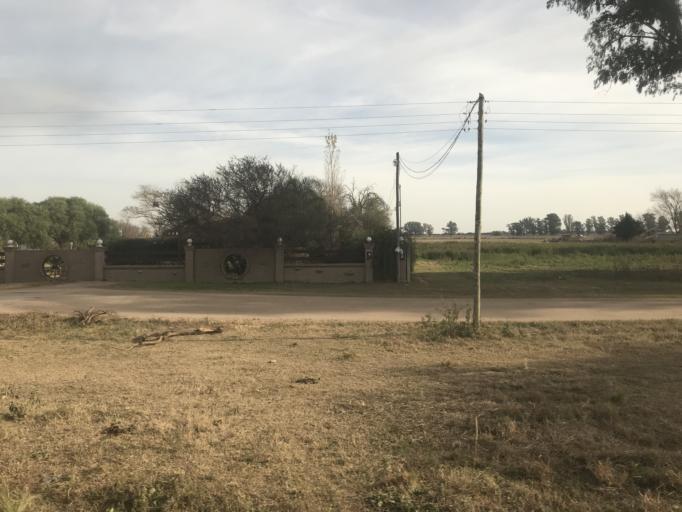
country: AR
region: Cordoba
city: Pilar
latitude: -31.6741
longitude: -63.8928
